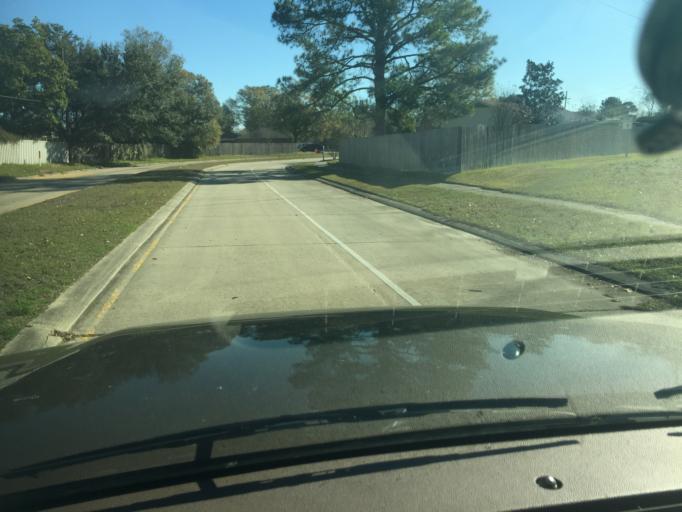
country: US
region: Louisiana
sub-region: Saint Tammany Parish
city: Slidell
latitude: 30.3017
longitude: -89.7685
